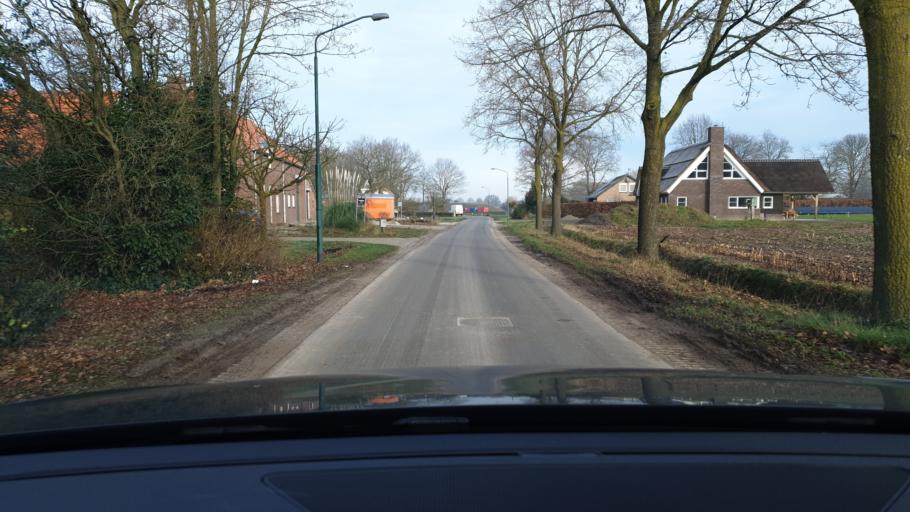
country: NL
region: North Brabant
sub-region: Gemeente Veldhoven
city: Oerle
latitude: 51.4348
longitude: 5.3438
